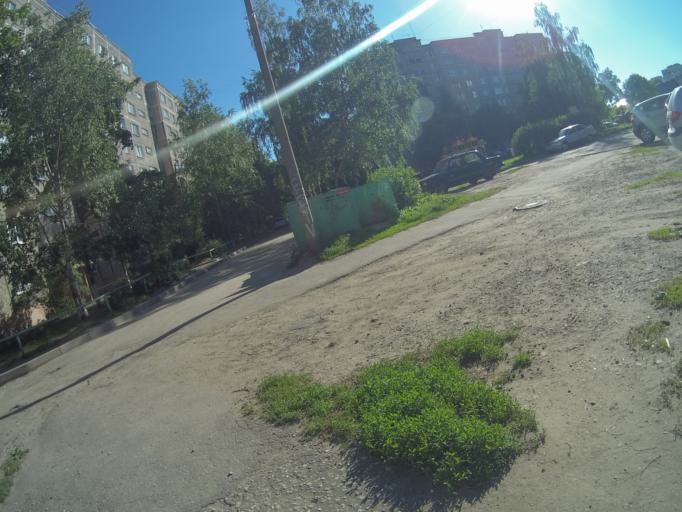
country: RU
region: Vladimir
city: Kommunar
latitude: 56.1602
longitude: 40.4687
